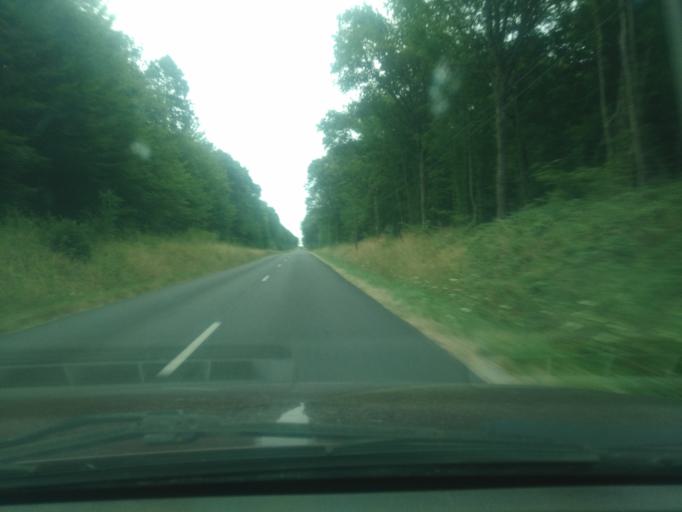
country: FR
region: Bourgogne
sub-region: Departement de la Nievre
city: Dornes
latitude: 46.7754
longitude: 3.2850
